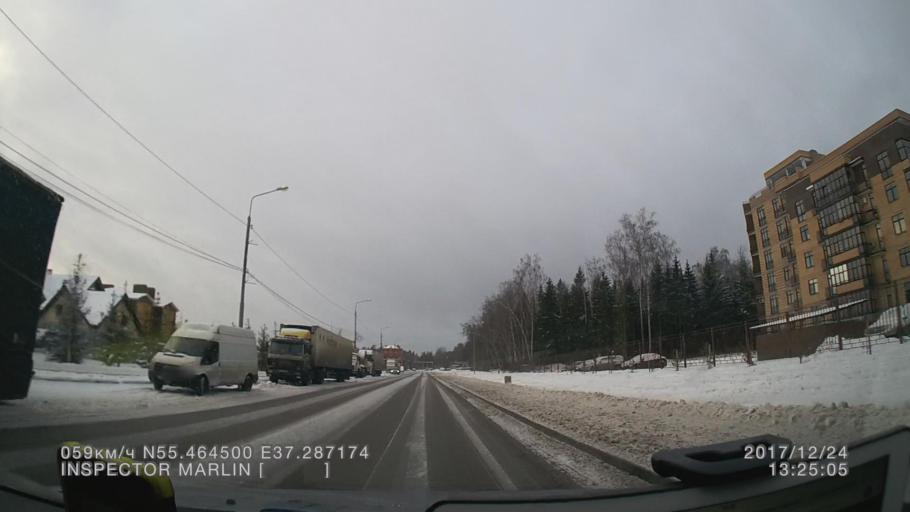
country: RU
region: Moskovskaya
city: Troitsk
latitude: 55.4645
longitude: 37.2870
